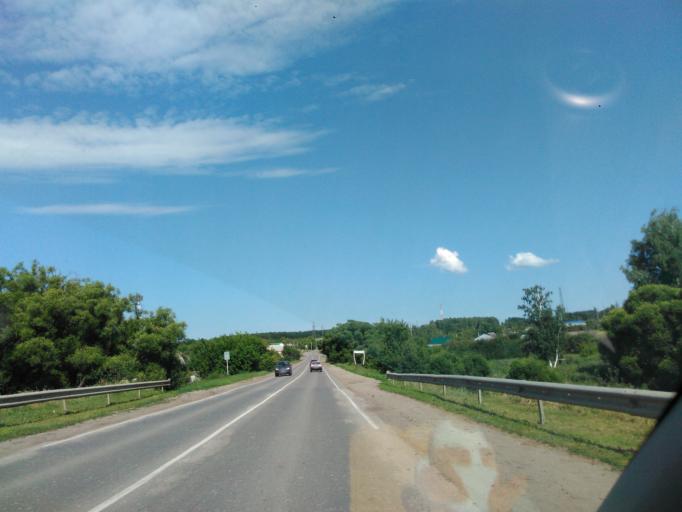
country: RU
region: Penza
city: Belinskiy
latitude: 52.9663
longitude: 43.4370
